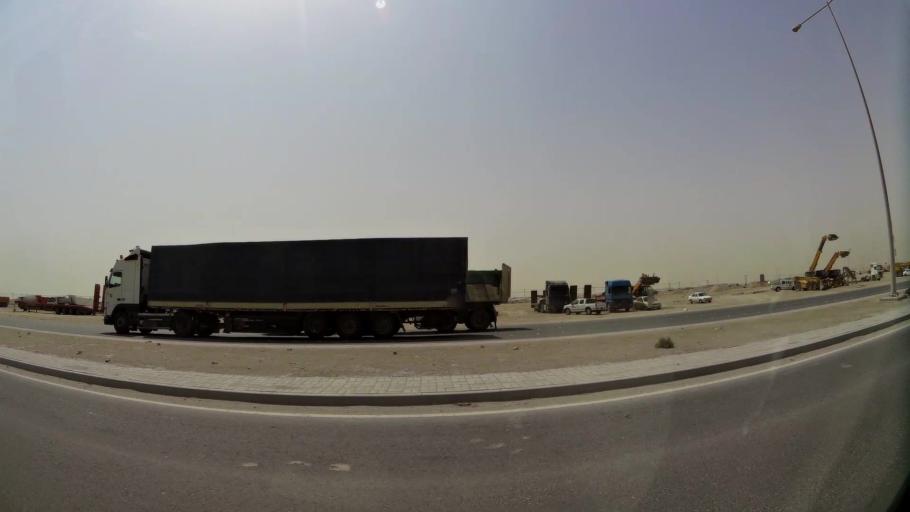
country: QA
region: Baladiyat ar Rayyan
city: Ar Rayyan
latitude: 25.1793
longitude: 51.4011
